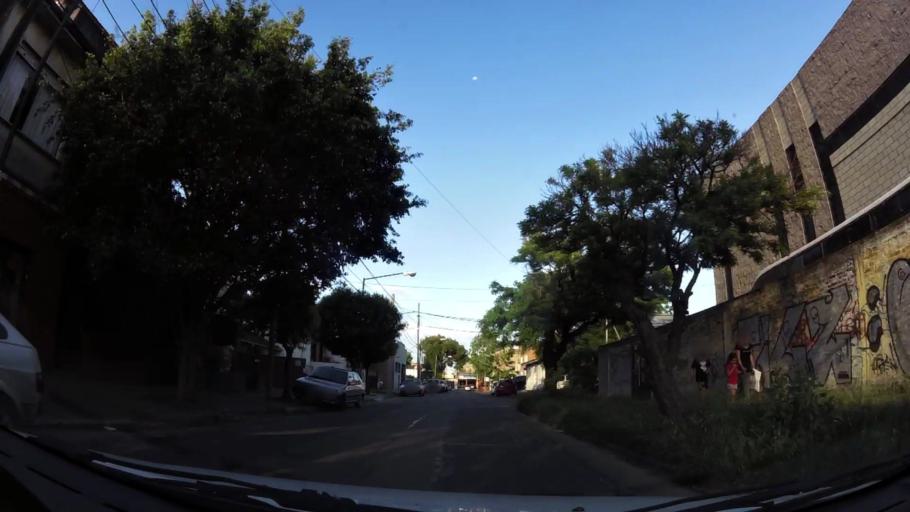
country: AR
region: Buenos Aires
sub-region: Partido de San Isidro
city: San Isidro
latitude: -34.4668
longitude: -58.5446
